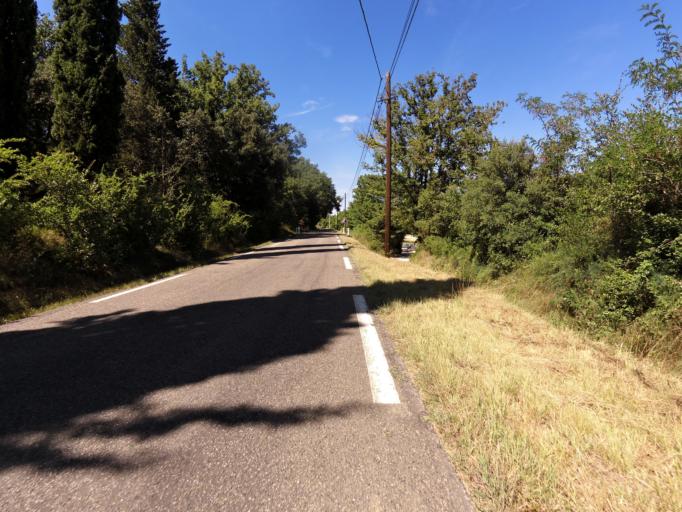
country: FR
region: Languedoc-Roussillon
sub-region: Departement du Gard
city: Sommieres
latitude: 43.8192
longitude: 4.0691
